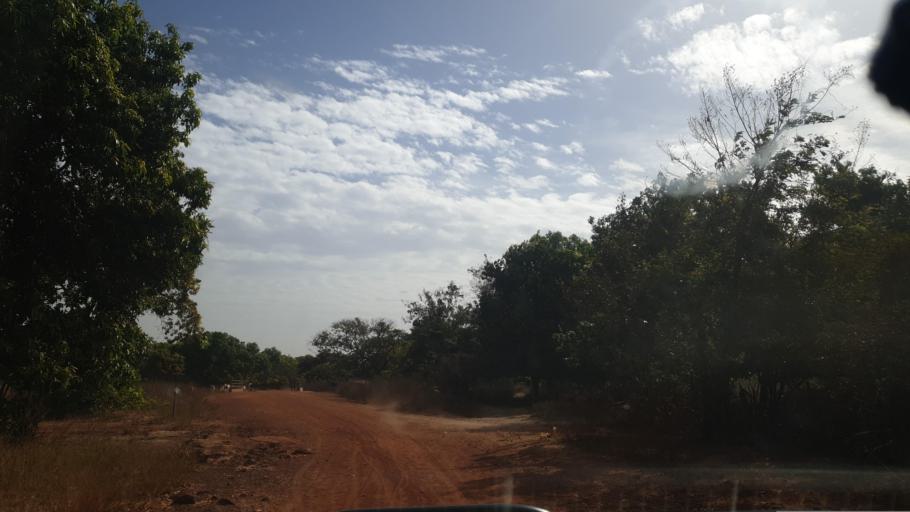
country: ML
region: Sikasso
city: Yanfolila
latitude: 11.4178
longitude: -7.9925
